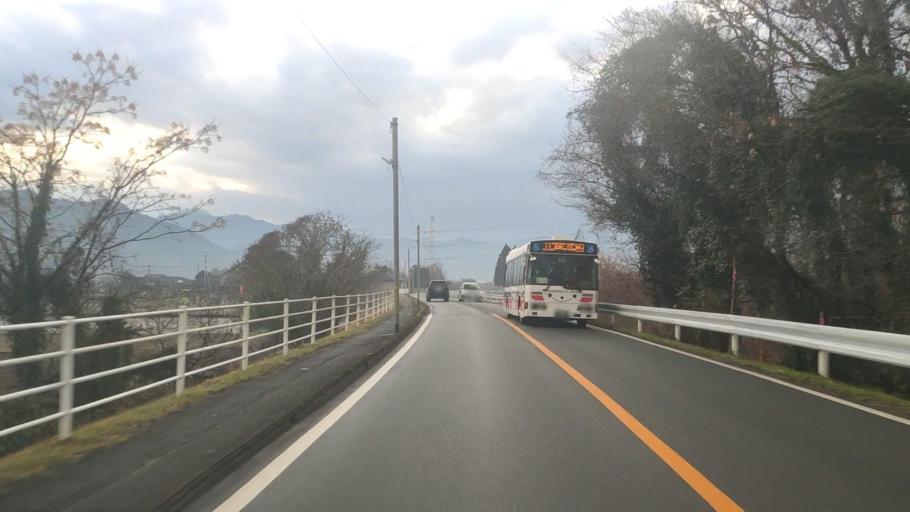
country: JP
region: Kumamoto
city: Uto
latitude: 32.6904
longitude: 130.7937
